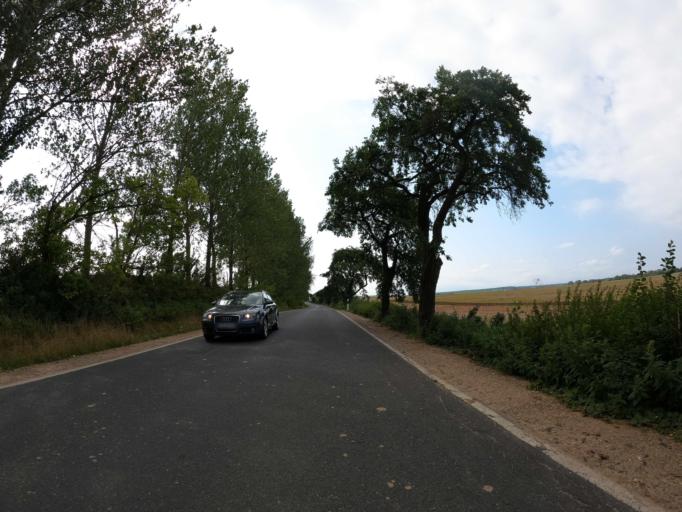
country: DE
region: Mecklenburg-Vorpommern
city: Malchow
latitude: 53.4431
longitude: 12.5073
